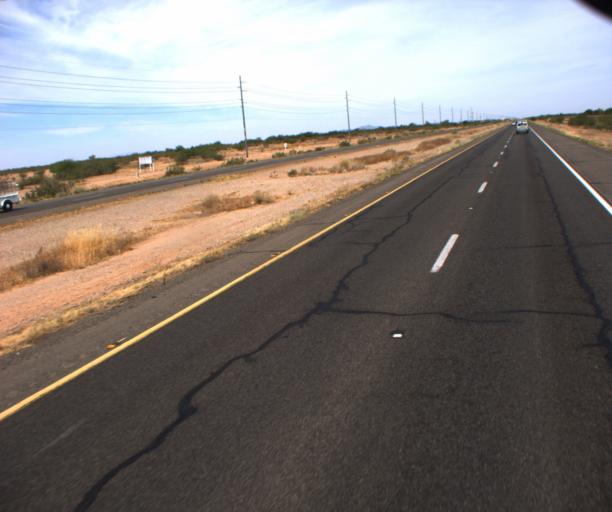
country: US
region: Arizona
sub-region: Maricopa County
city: Sun City West
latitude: 33.7186
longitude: -112.4524
